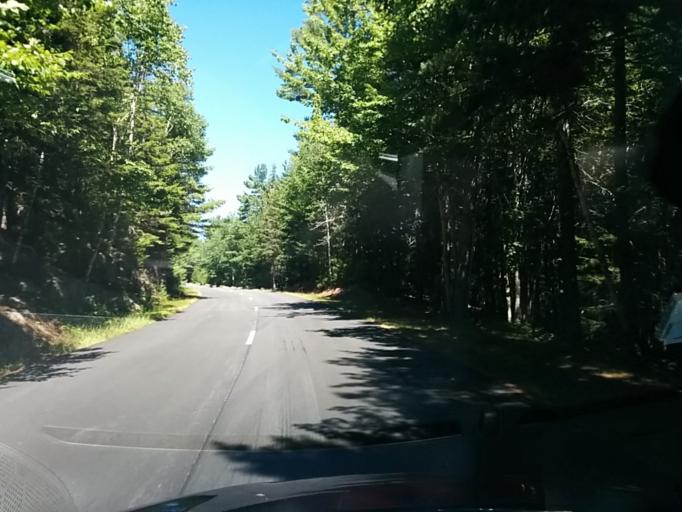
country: US
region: Maine
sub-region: Hancock County
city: Bar Harbor
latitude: 44.3152
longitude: -68.2259
